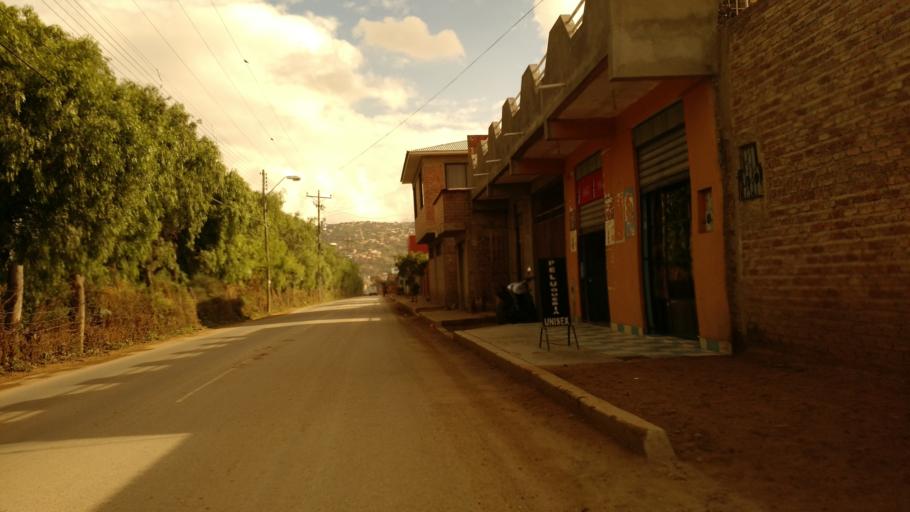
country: BO
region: Cochabamba
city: Cochabamba
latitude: -17.4552
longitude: -66.1427
